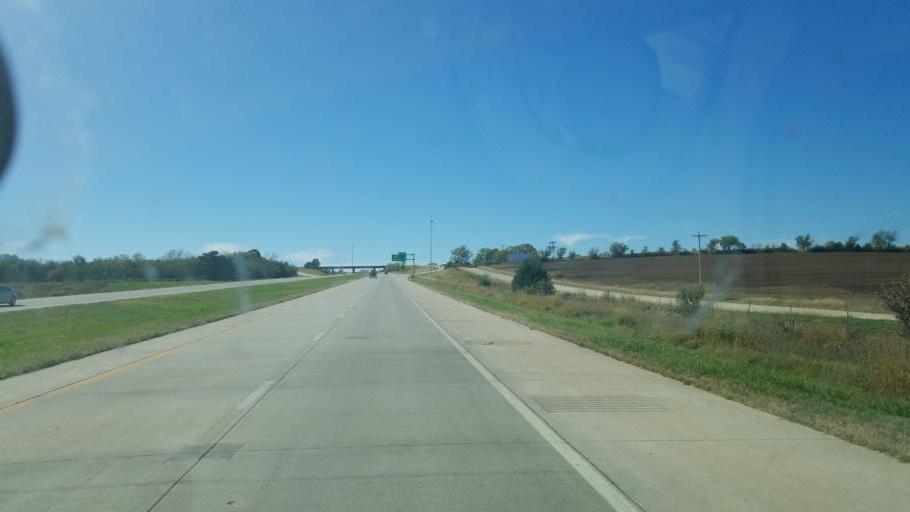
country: US
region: Kansas
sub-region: Riley County
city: Ogden
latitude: 39.0608
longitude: -96.7340
